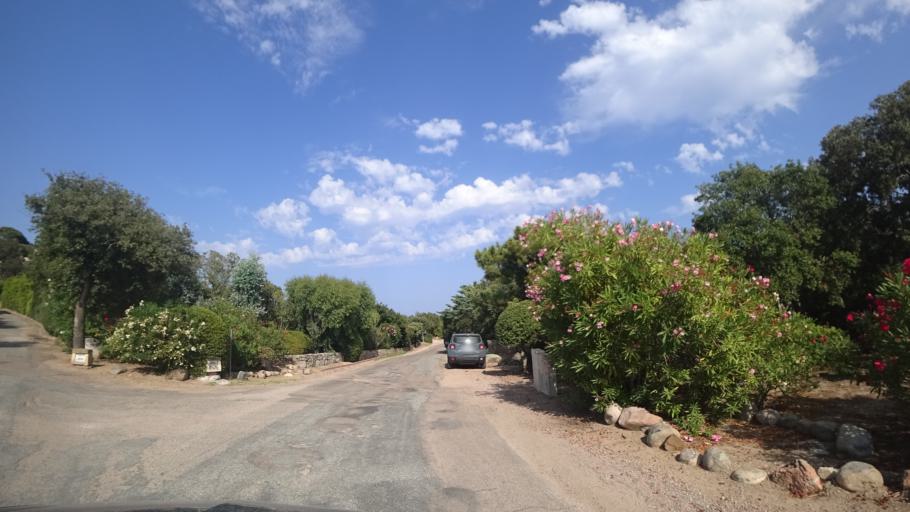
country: FR
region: Corsica
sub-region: Departement de la Corse-du-Sud
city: Porto-Vecchio
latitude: 41.6198
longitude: 9.3495
